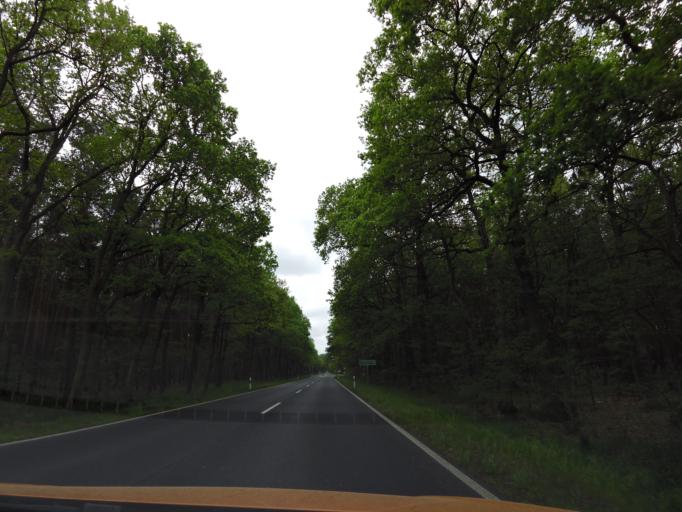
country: DE
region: Brandenburg
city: Beelitz
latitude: 52.2042
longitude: 12.9586
